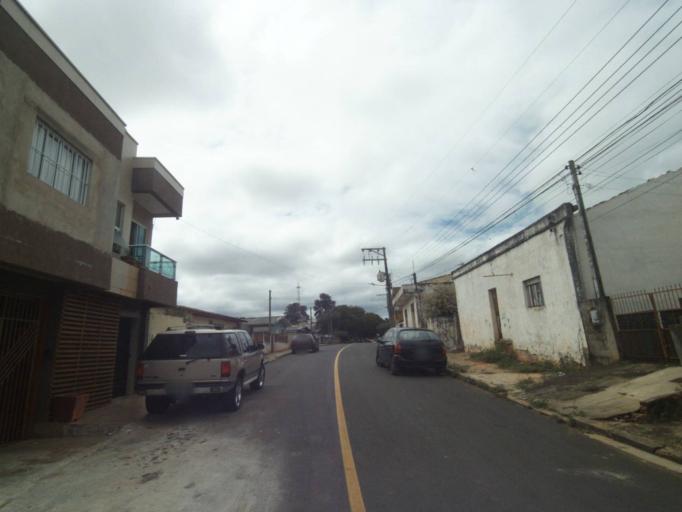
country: BR
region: Parana
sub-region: Telemaco Borba
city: Telemaco Borba
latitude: -24.3265
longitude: -50.6284
